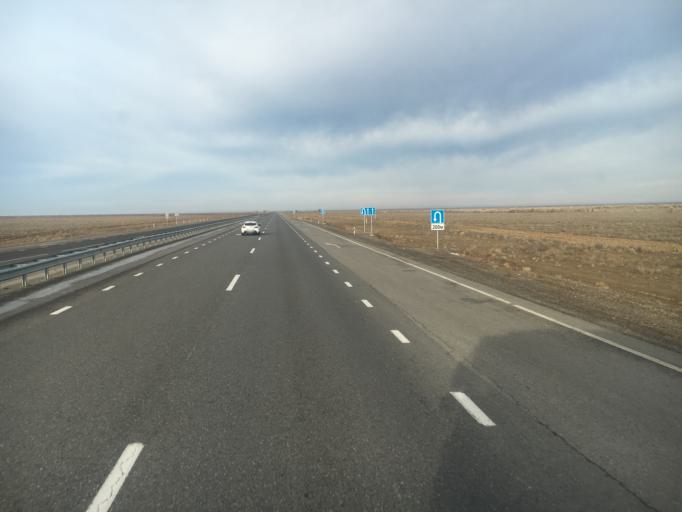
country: KZ
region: Ongtustik Qazaqstan
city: Turkestan
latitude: 43.5172
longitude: 67.8114
